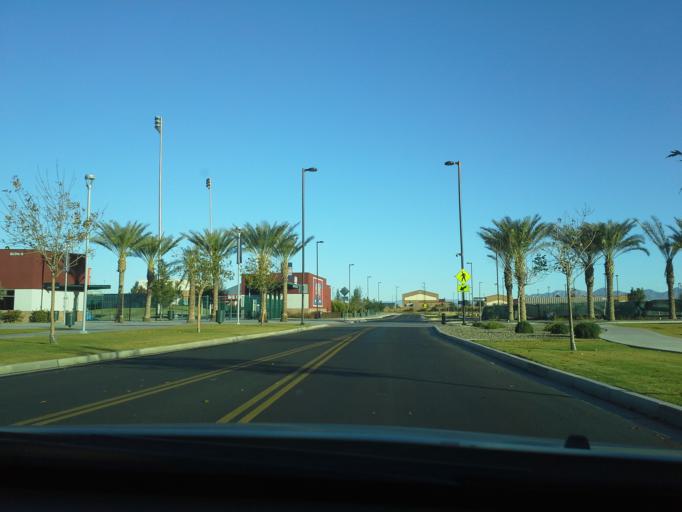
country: US
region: Arizona
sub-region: Maricopa County
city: Tempe
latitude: 33.4302
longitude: -111.8802
